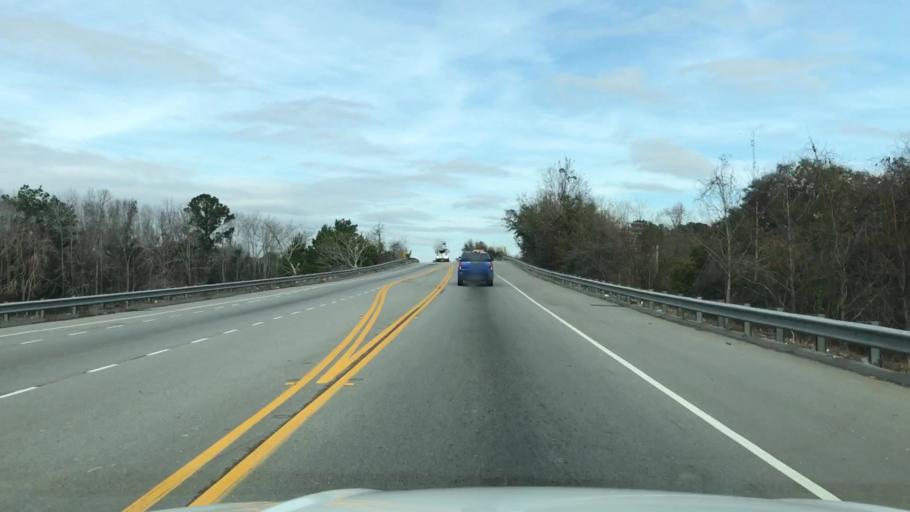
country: US
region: South Carolina
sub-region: Charleston County
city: Shell Point
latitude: 32.7912
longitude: -80.1079
